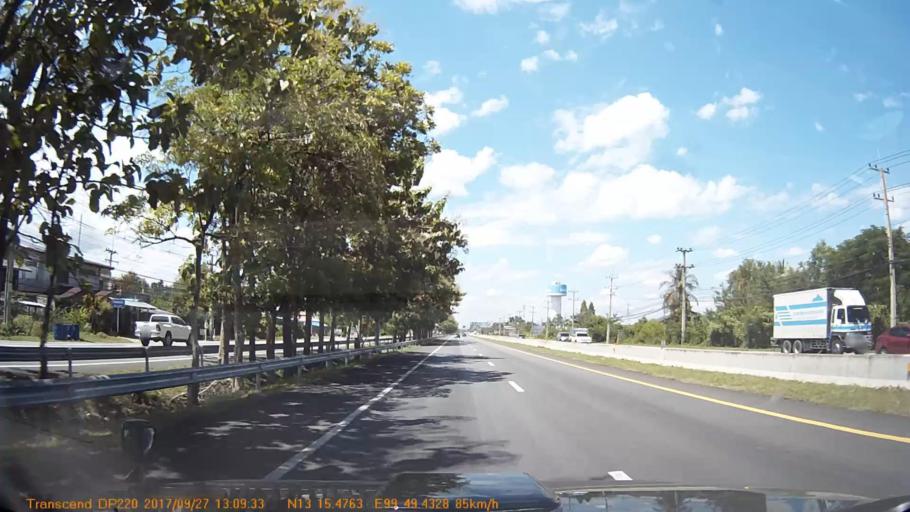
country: TH
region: Phetchaburi
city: Khao Yoi
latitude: 13.2579
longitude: 99.8239
